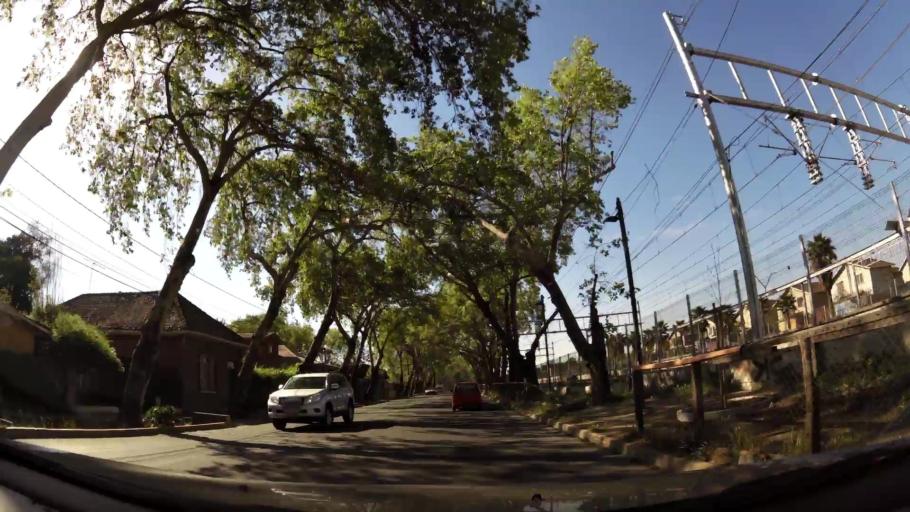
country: CL
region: Santiago Metropolitan
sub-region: Provincia de Maipo
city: San Bernardo
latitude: -33.6064
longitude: -70.6972
